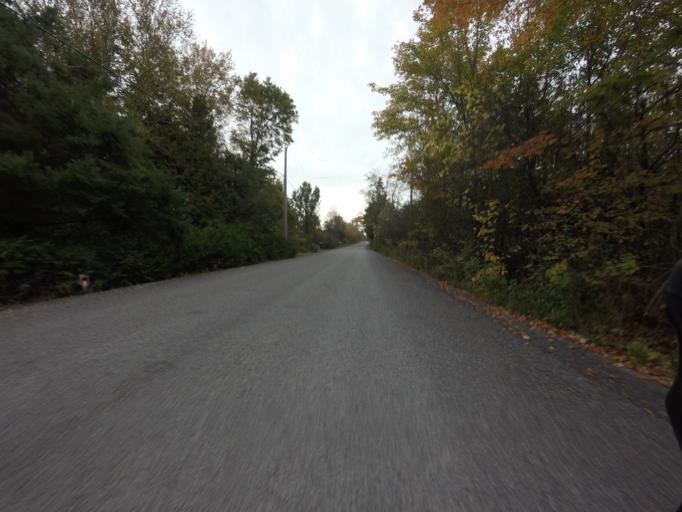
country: CA
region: Ontario
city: Bells Corners
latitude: 45.0762
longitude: -75.7571
